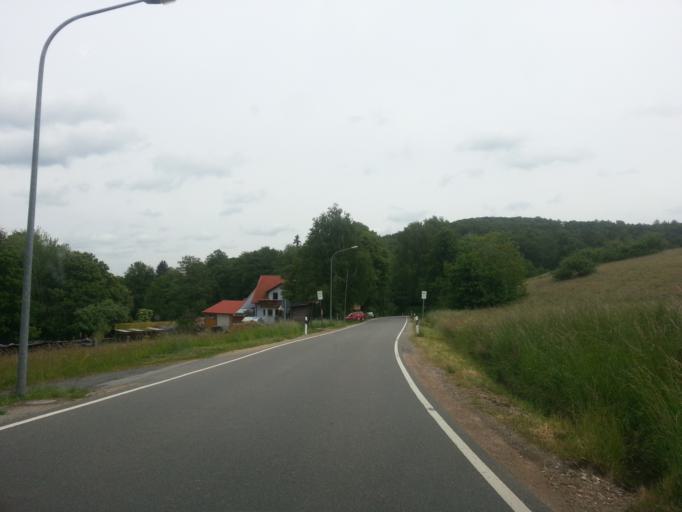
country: DE
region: Hesse
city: Lutzelbach
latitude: 49.7411
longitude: 8.7108
